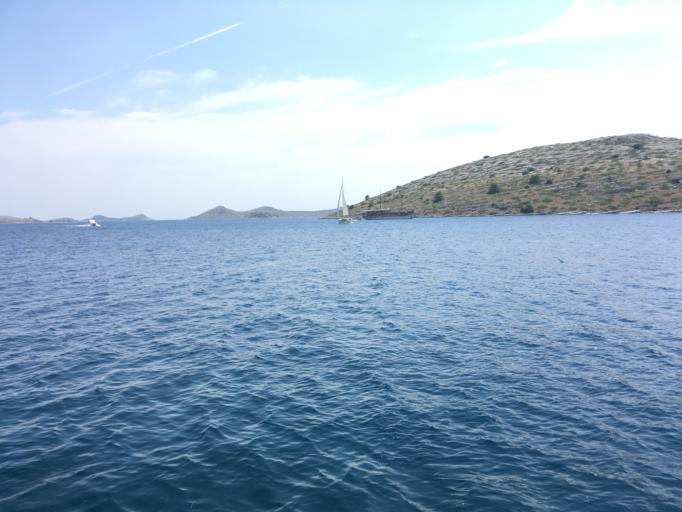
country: HR
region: Zadarska
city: Sali
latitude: 43.8281
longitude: 15.2629
